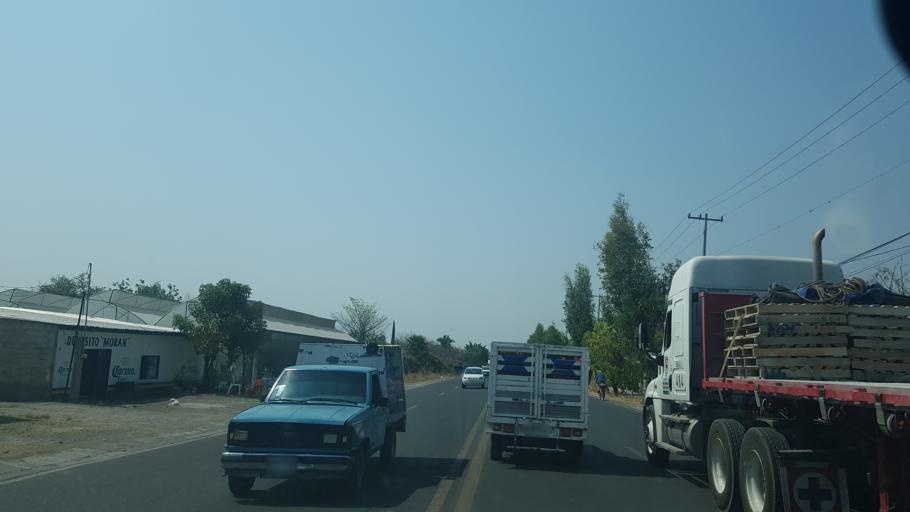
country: MX
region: Morelos
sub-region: Temoac
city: Temoac
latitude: 18.7677
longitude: -98.7791
